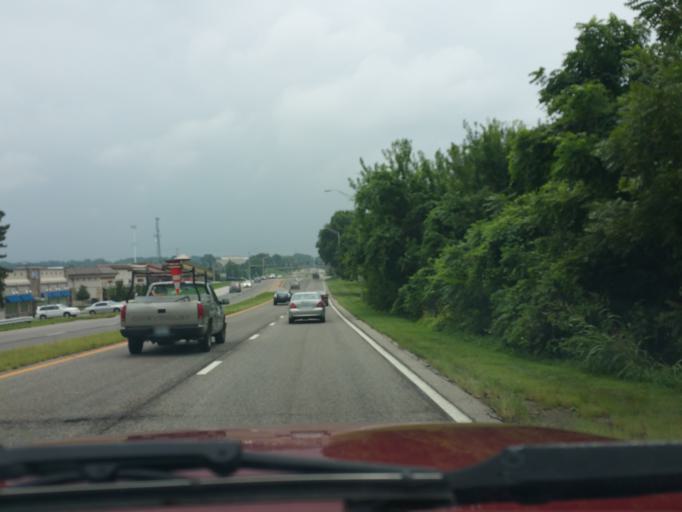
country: US
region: Kansas
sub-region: Johnson County
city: Mission
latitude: 39.0212
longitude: -94.6677
